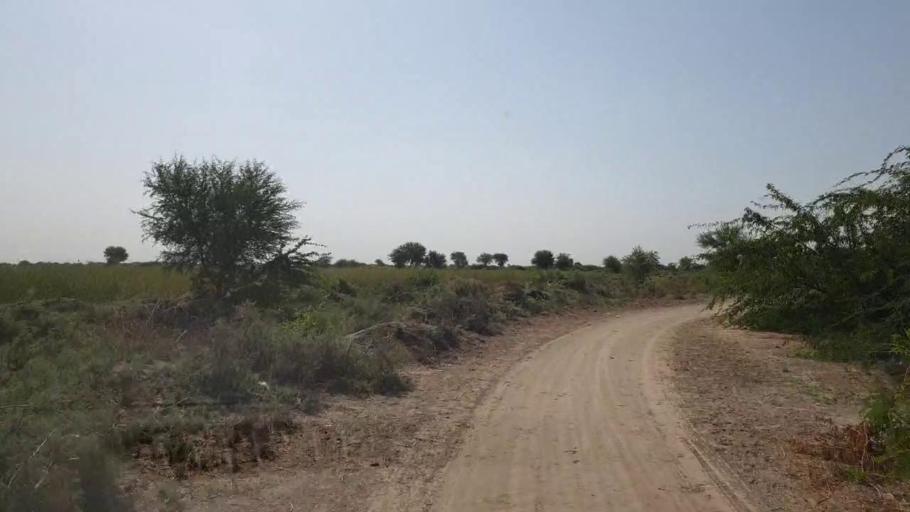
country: PK
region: Sindh
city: Tando Bago
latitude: 24.7369
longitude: 69.0222
